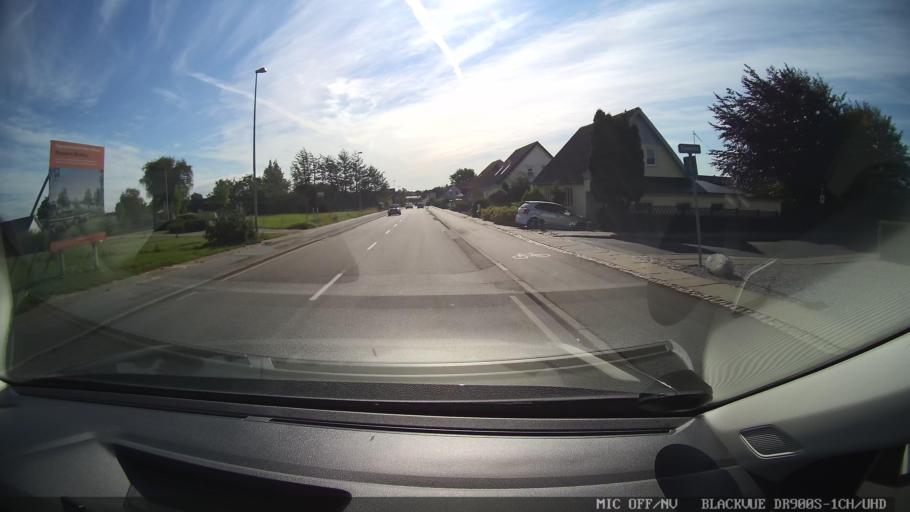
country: DK
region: North Denmark
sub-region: Mariagerfjord Kommune
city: Arden
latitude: 56.7708
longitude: 9.8526
